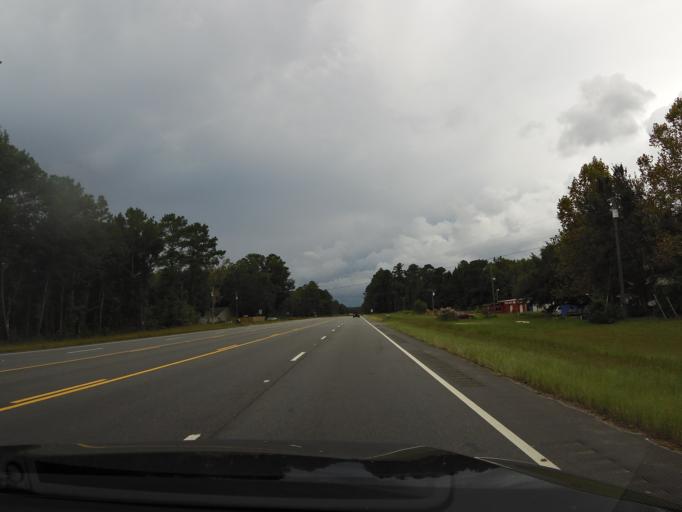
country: US
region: Georgia
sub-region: Glynn County
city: Dock Junction
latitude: 31.2862
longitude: -81.5664
